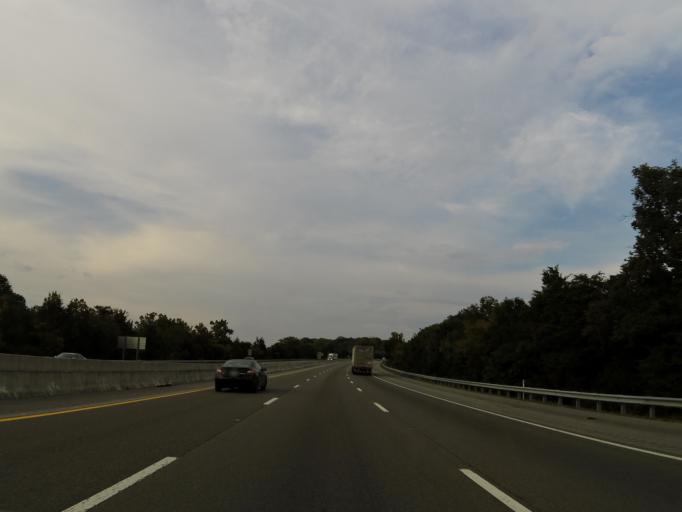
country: US
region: Tennessee
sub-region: Davidson County
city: Belle Meade
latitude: 36.1020
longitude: -86.9338
